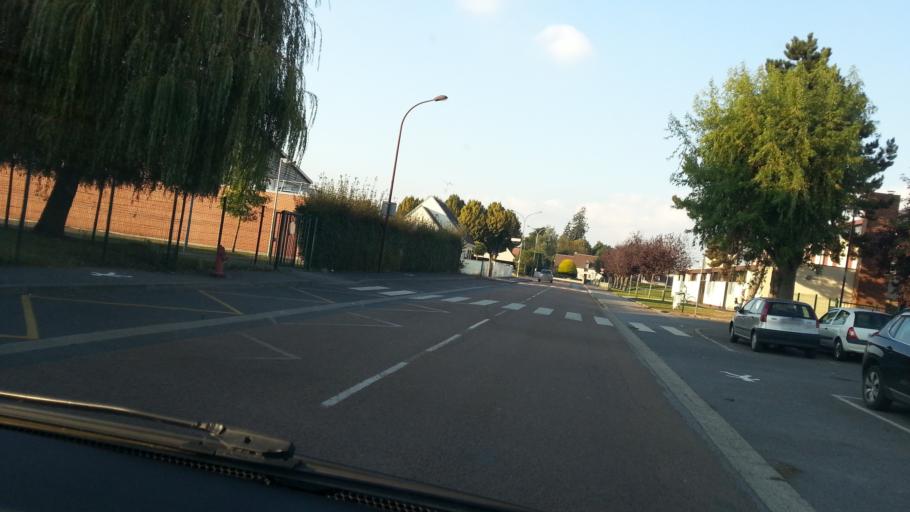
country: FR
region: Picardie
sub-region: Departement de l'Oise
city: Estrees-Saint-Denis
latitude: 49.4291
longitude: 2.6427
